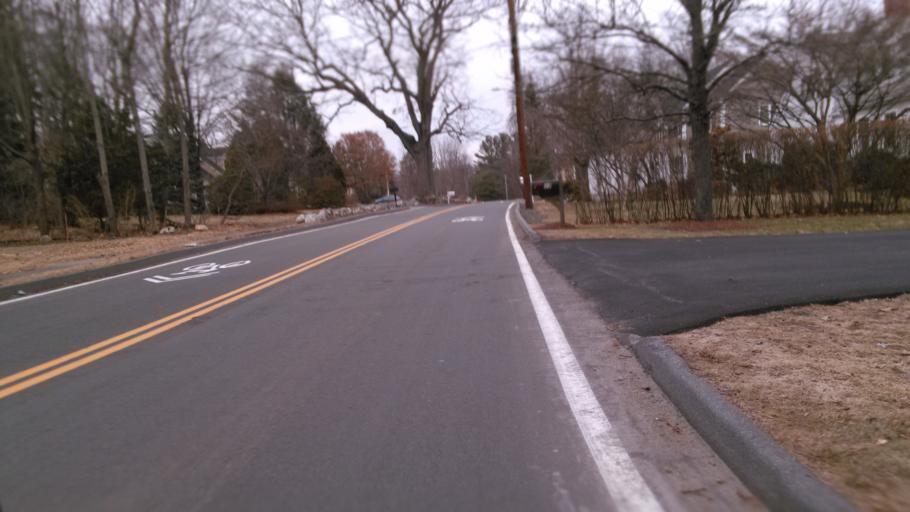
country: US
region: Massachusetts
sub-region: Middlesex County
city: Lexington
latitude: 42.4700
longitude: -71.2342
